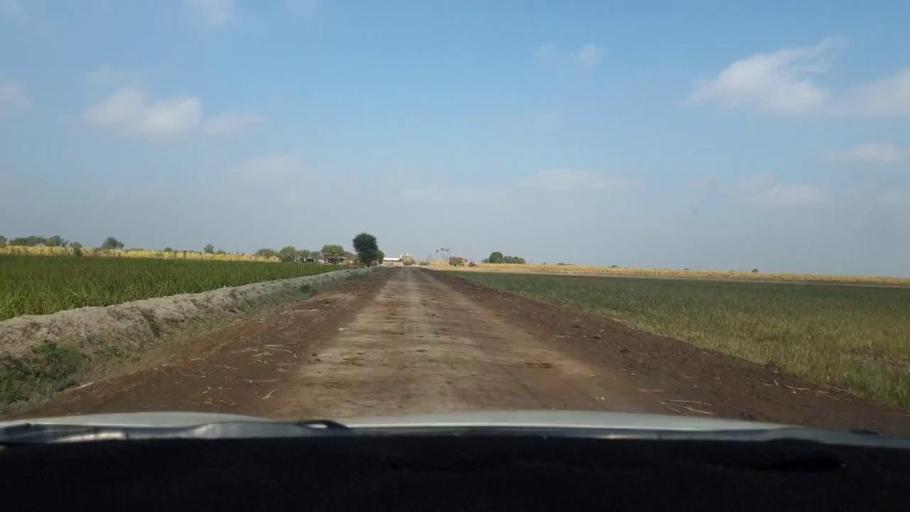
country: PK
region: Sindh
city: Berani
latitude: 25.7489
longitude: 69.0076
